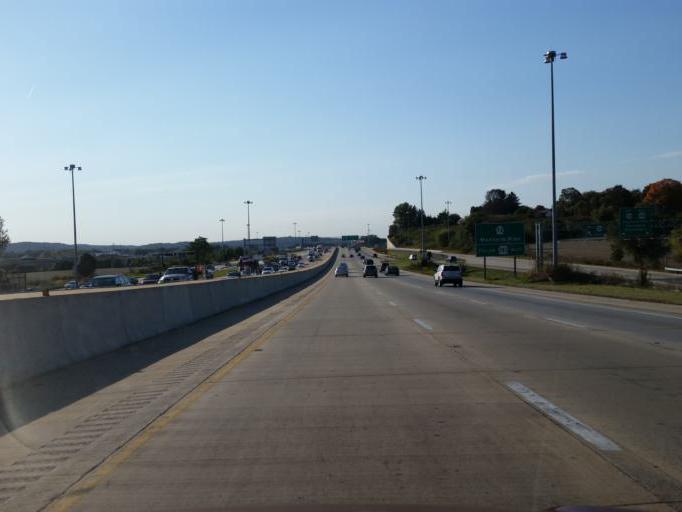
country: US
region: Pennsylvania
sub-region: Lancaster County
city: Lancaster
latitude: 40.0693
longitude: -76.3090
